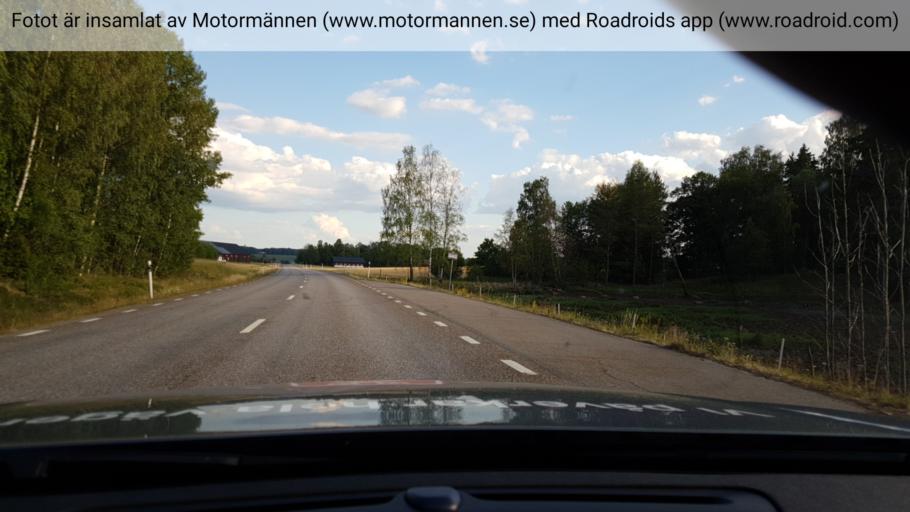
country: SE
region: Uppsala
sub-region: Heby Kommun
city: Morgongava
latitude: 59.8436
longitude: 16.9253
